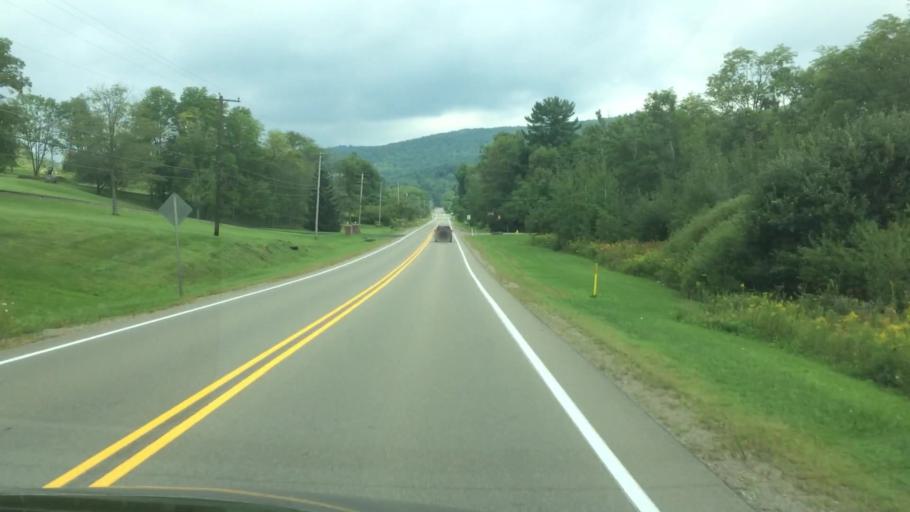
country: US
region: Pennsylvania
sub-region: McKean County
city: Bradford
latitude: 41.8942
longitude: -78.6070
